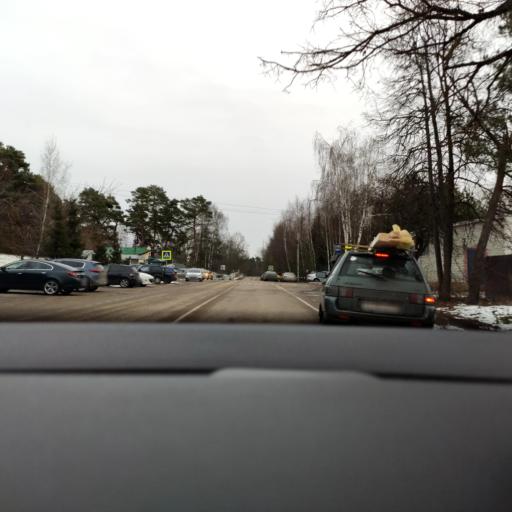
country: RU
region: Moskovskaya
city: Zvenigorod
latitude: 55.7110
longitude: 36.8896
